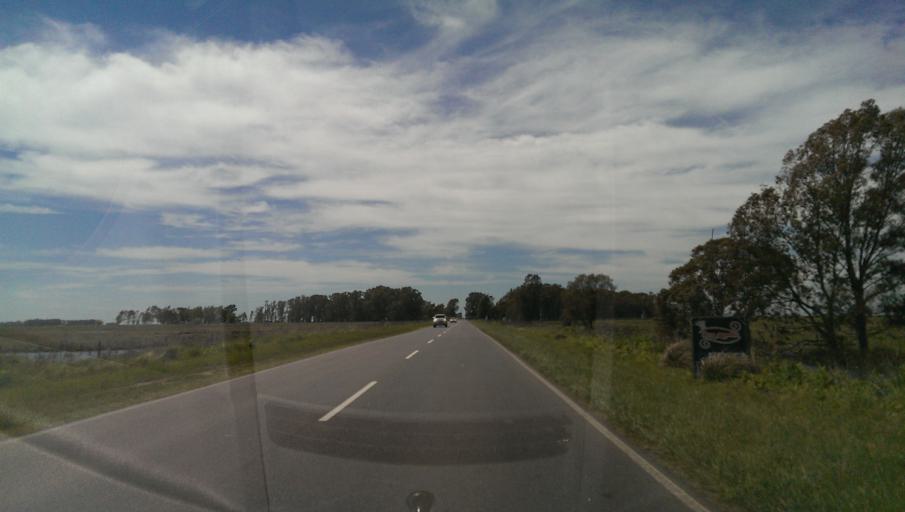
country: AR
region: Buenos Aires
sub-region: Partido de Laprida
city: Laprida
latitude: -37.3826
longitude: -60.9916
